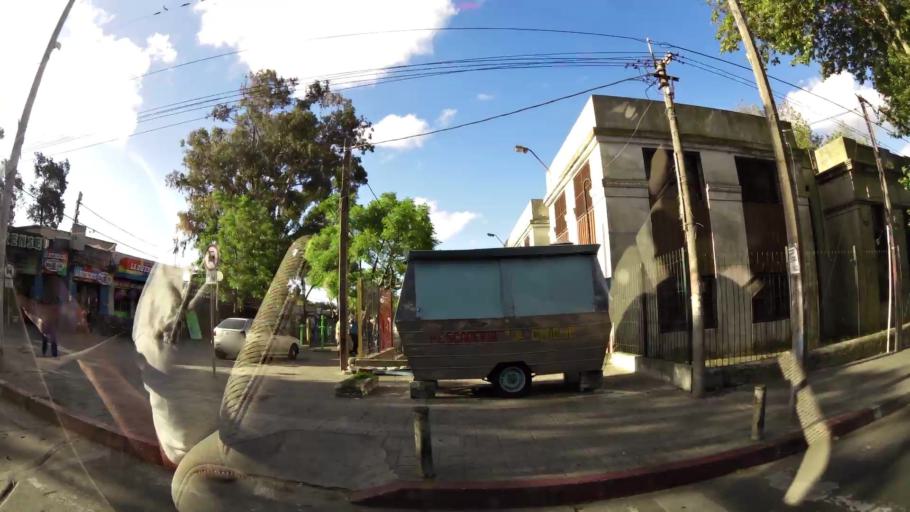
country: UY
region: Montevideo
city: Montevideo
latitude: -34.8739
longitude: -56.2501
